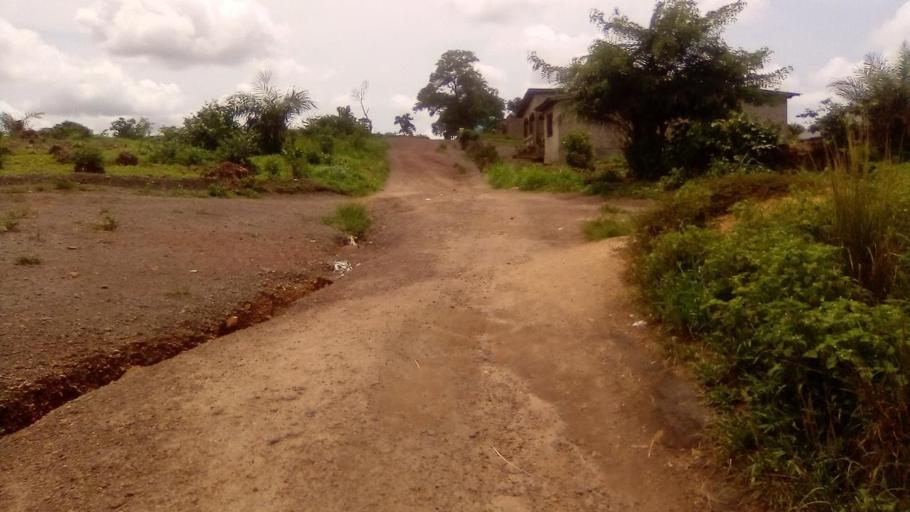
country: SL
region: Southern Province
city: Bo
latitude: 7.9353
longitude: -11.7387
